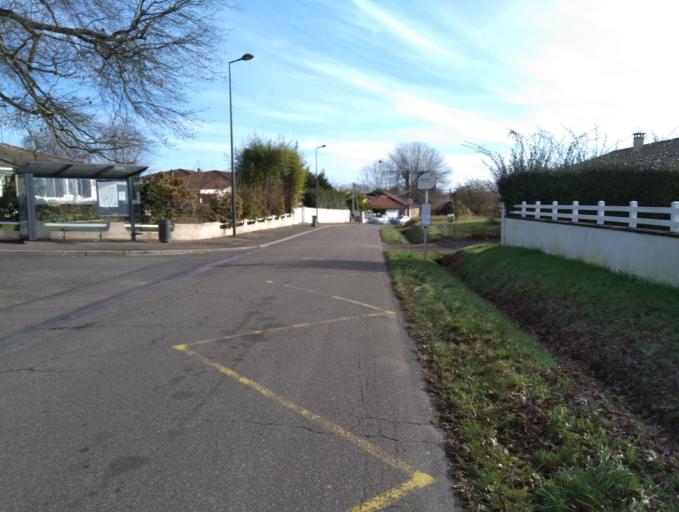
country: FR
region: Aquitaine
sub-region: Departement des Landes
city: Oeyreluy
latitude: 43.6752
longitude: -1.0820
